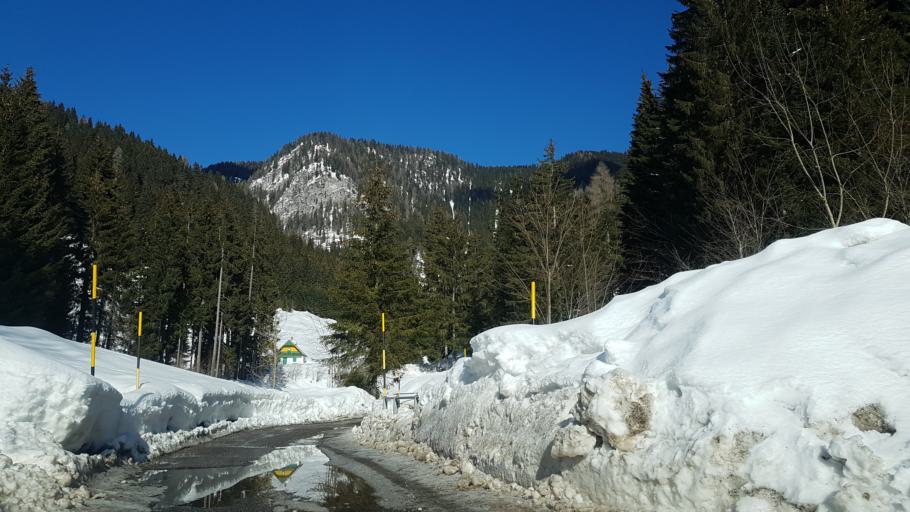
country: IT
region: Friuli Venezia Giulia
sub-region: Provincia di Udine
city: Malborghetto
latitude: 46.5481
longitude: 13.4789
